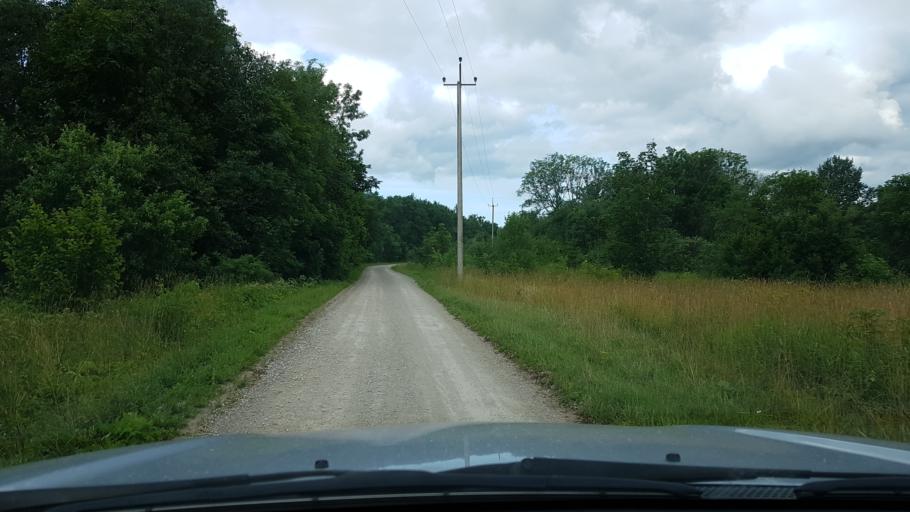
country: EE
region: Ida-Virumaa
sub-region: Narva-Joesuu linn
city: Narva-Joesuu
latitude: 59.4086
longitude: 27.9821
